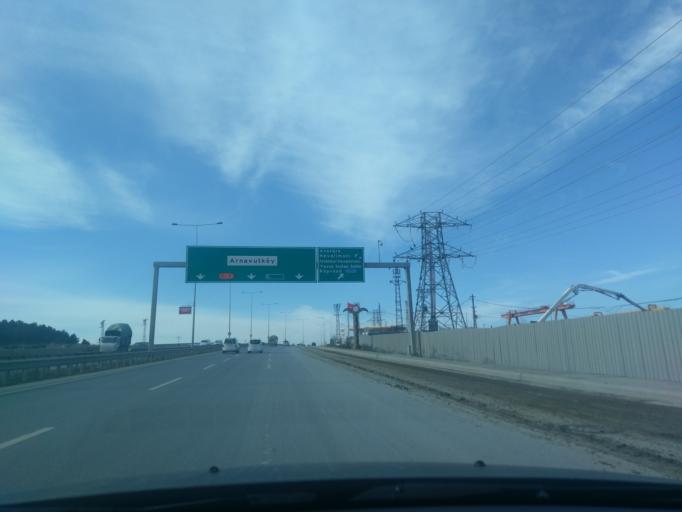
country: TR
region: Istanbul
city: Basaksehir
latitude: 41.1364
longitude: 28.8140
